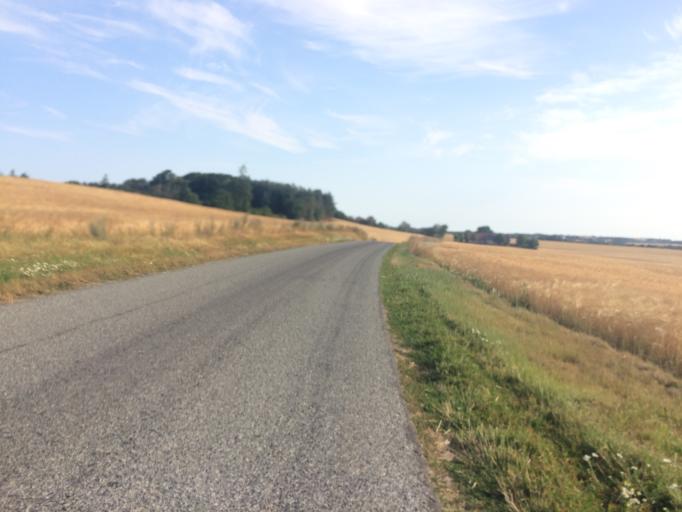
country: DK
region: Central Jutland
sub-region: Holstebro Kommune
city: Vinderup
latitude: 56.6037
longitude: 8.7608
